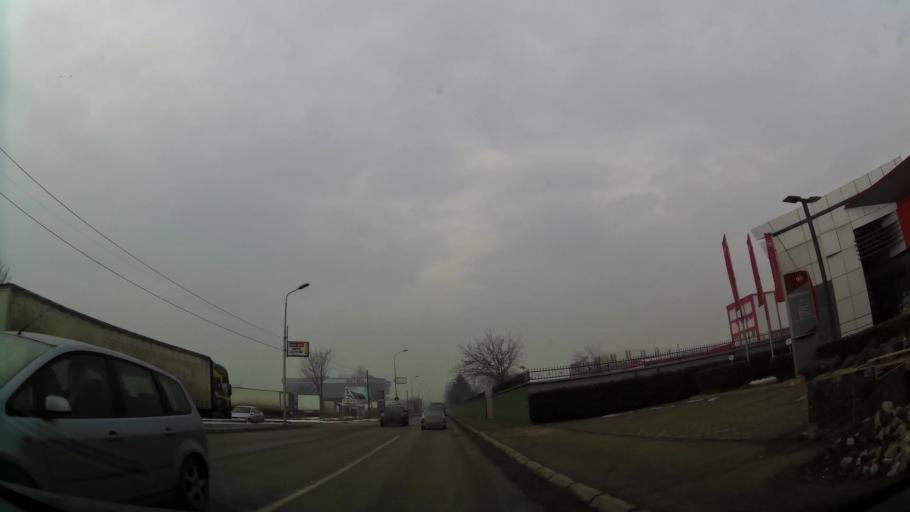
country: MK
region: Kisela Voda
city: Usje
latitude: 41.9970
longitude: 21.4828
